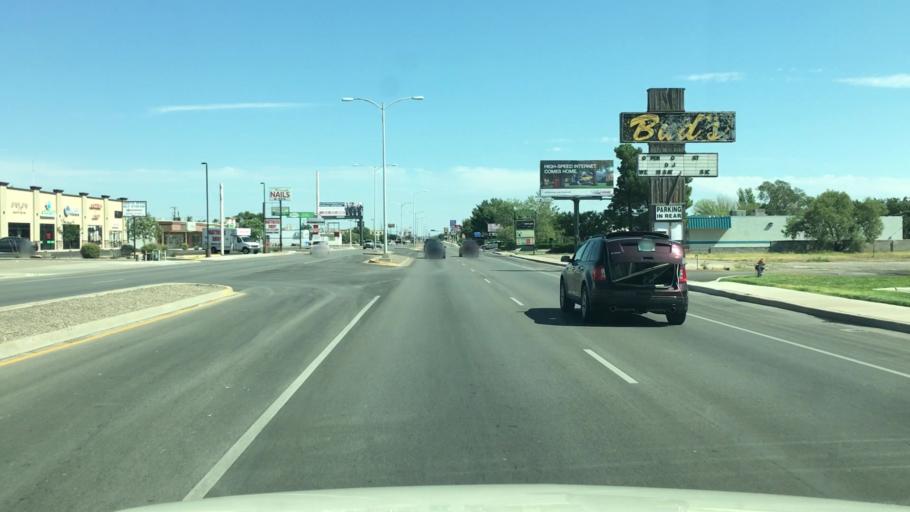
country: US
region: New Mexico
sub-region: Chaves County
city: Roswell
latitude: 33.4339
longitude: -104.5231
